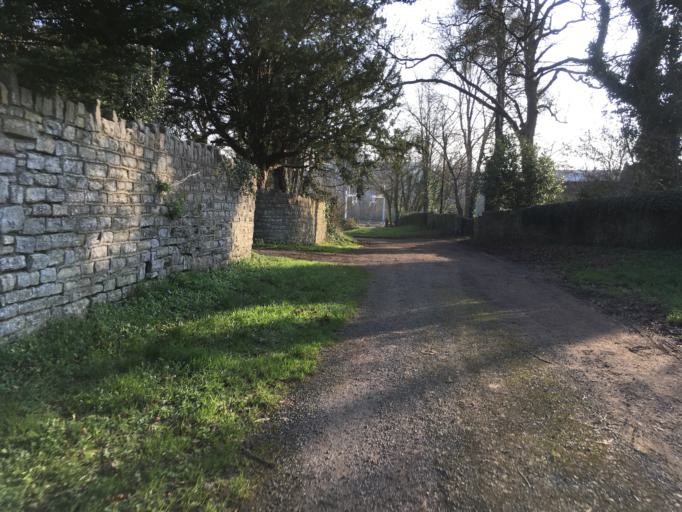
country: GB
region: Wales
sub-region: Newport
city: Bishton
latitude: 51.5817
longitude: -2.8867
